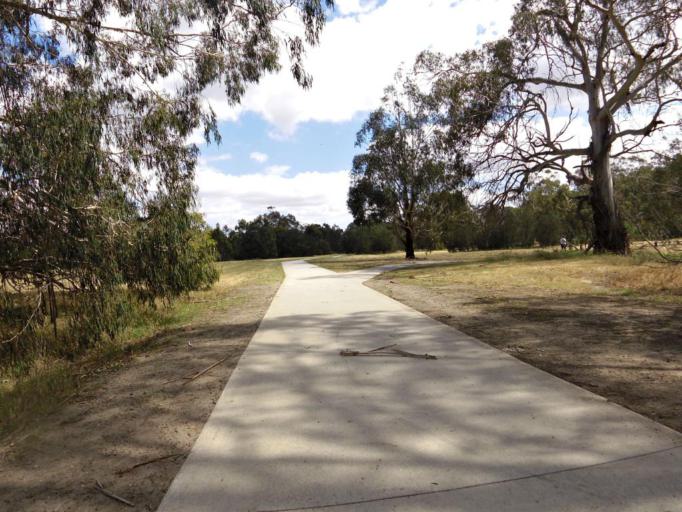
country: AU
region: Victoria
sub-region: Nillumbik
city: Eltham North
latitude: -37.6837
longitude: 145.1526
